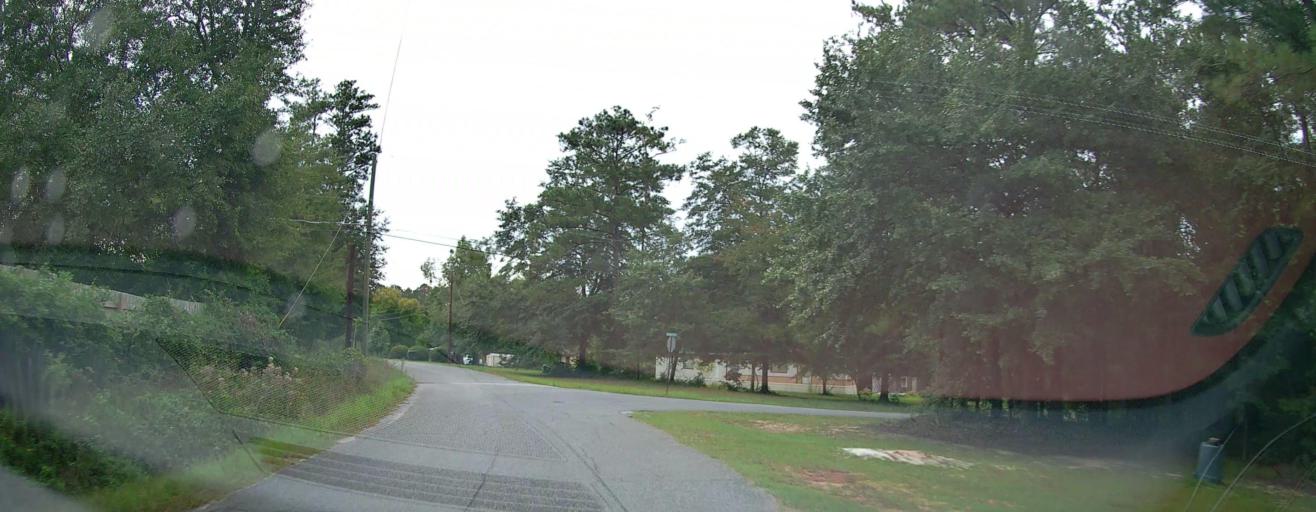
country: US
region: Georgia
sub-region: Peach County
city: Byron
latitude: 32.6778
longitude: -83.7137
